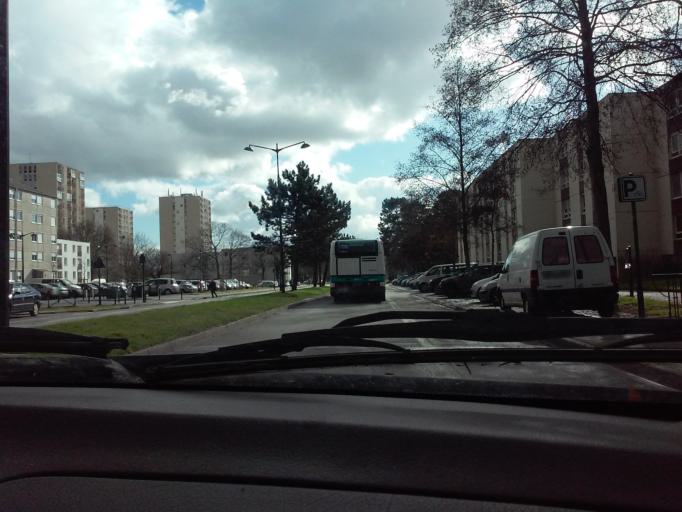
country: FR
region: Brittany
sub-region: Departement d'Ille-et-Vilaine
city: Rennes
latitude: 48.0892
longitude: -1.6823
